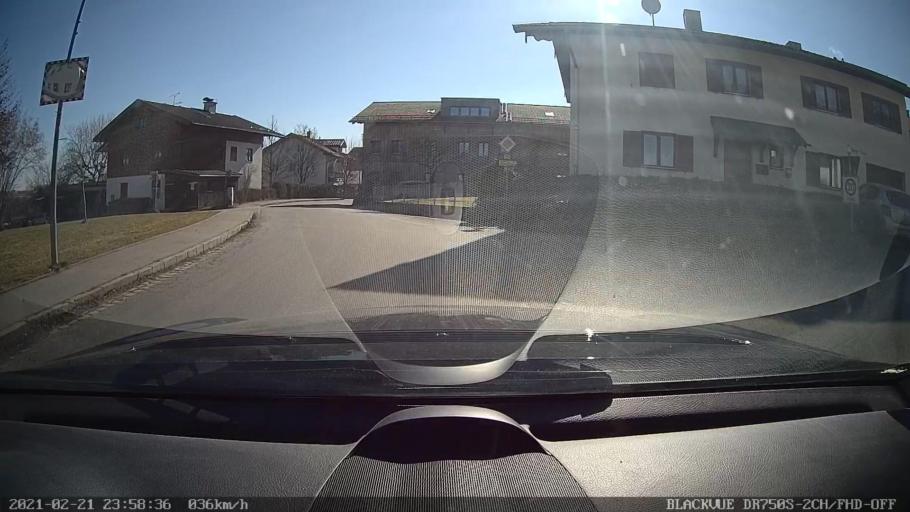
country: DE
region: Bavaria
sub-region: Upper Bavaria
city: Griesstatt
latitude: 47.9916
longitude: 12.1785
